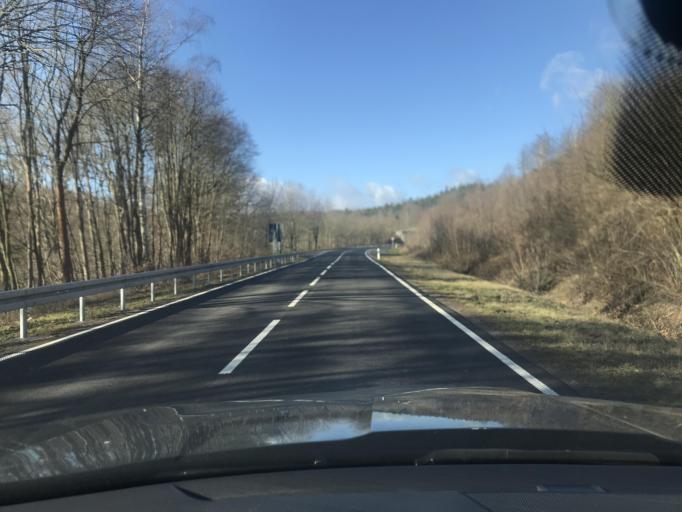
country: DE
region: Saxony-Anhalt
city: Huttenrode
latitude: 51.7832
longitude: 10.9188
